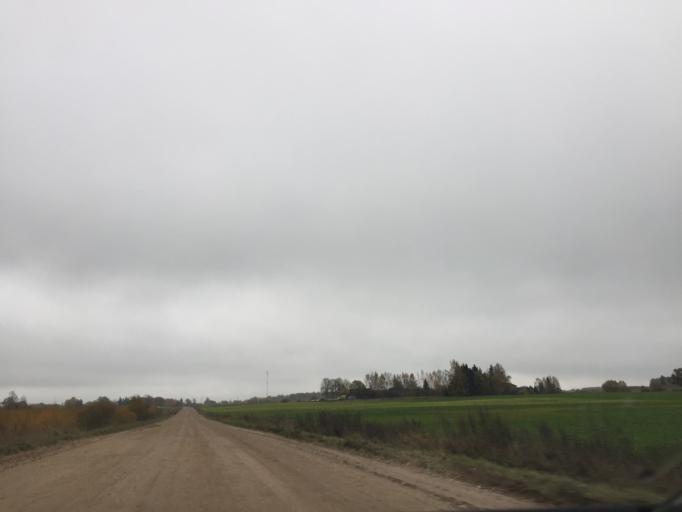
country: LV
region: Sigulda
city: Sigulda
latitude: 57.2719
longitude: 24.8511
